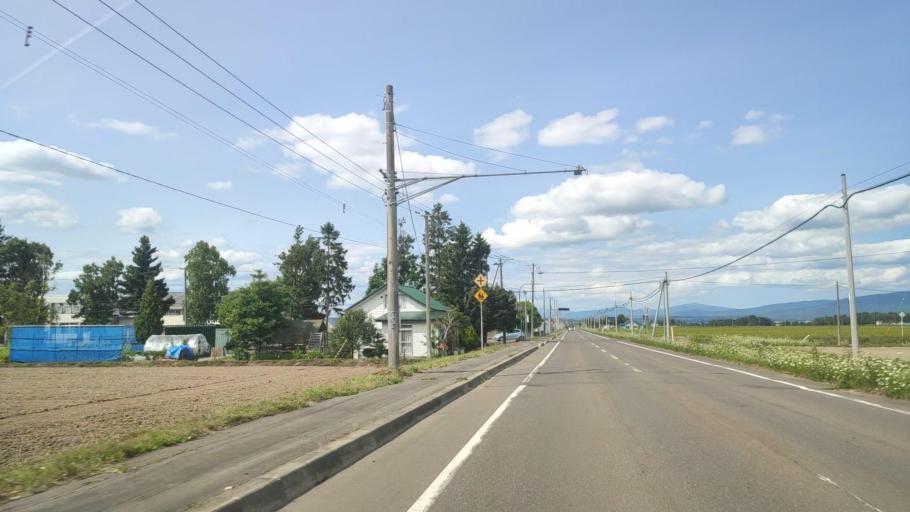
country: JP
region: Hokkaido
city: Nayoro
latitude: 44.2905
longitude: 142.4294
